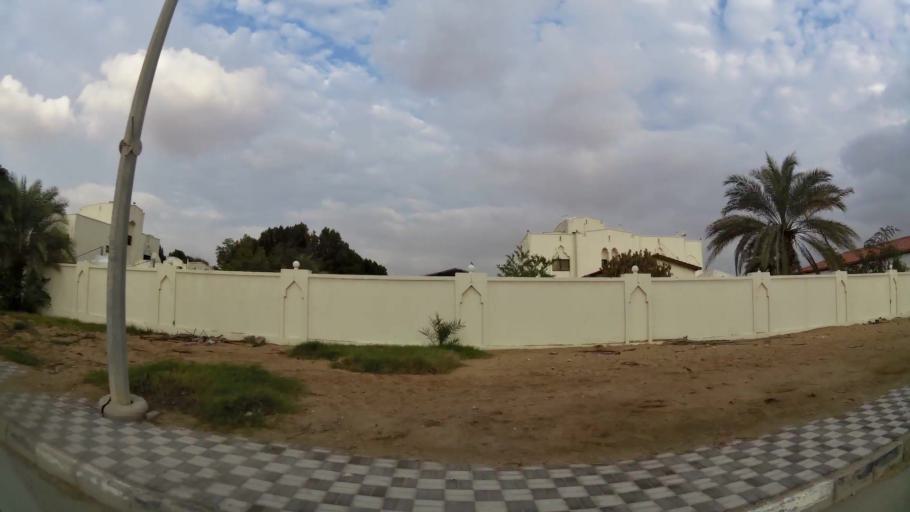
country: AE
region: Abu Dhabi
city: Abu Dhabi
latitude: 24.3868
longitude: 54.5306
